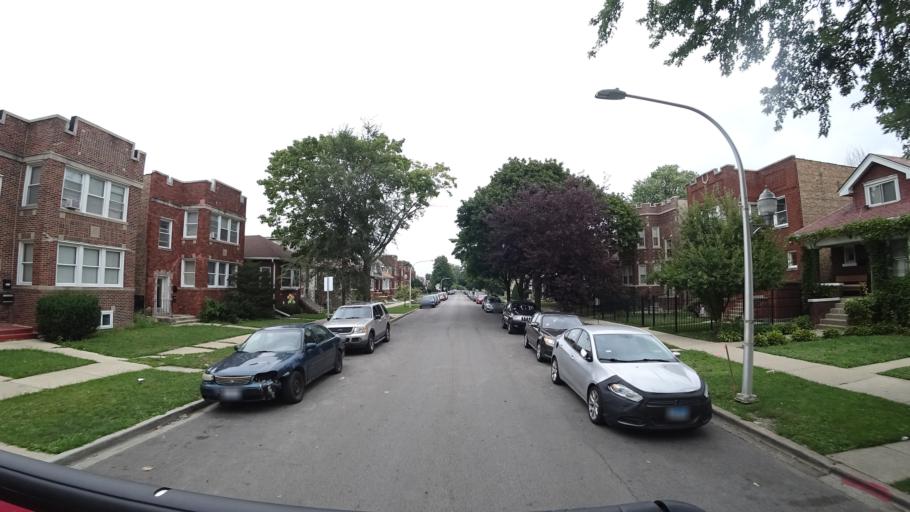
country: US
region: Illinois
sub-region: Cook County
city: Oak Park
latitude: 41.8681
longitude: -87.7730
